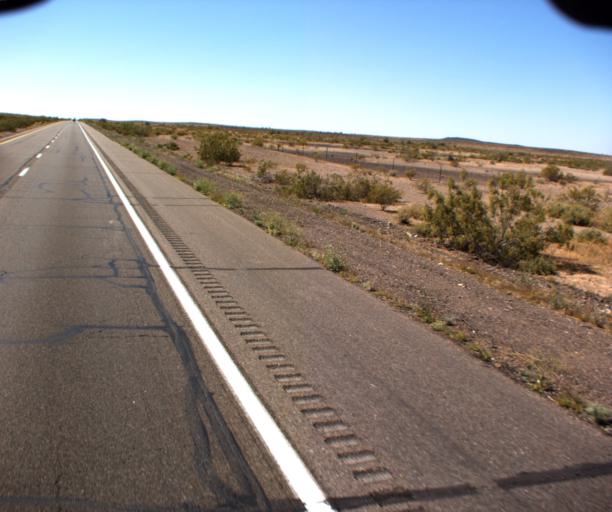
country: US
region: Arizona
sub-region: Maricopa County
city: Gila Bend
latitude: 32.8929
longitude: -113.0437
